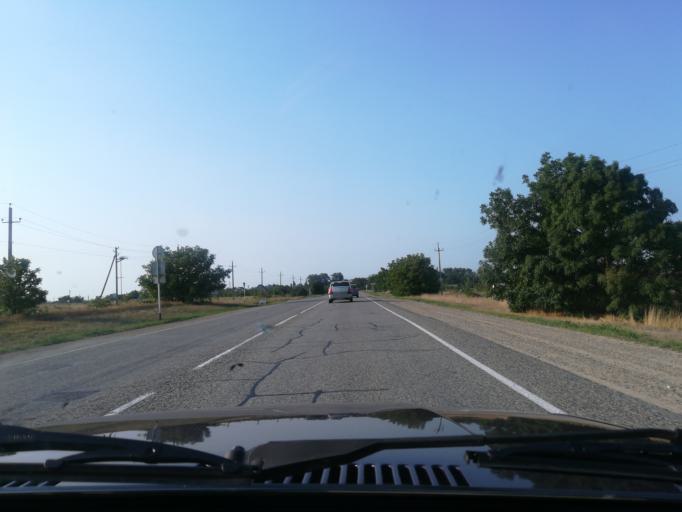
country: RU
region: Krasnodarskiy
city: Yurovka
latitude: 45.1080
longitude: 37.4219
